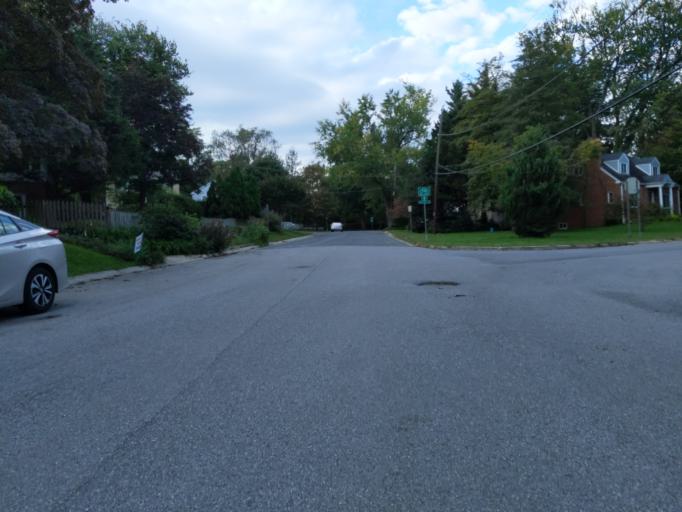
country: US
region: Maryland
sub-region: Montgomery County
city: Forest Glen
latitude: 39.0119
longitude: -77.0435
